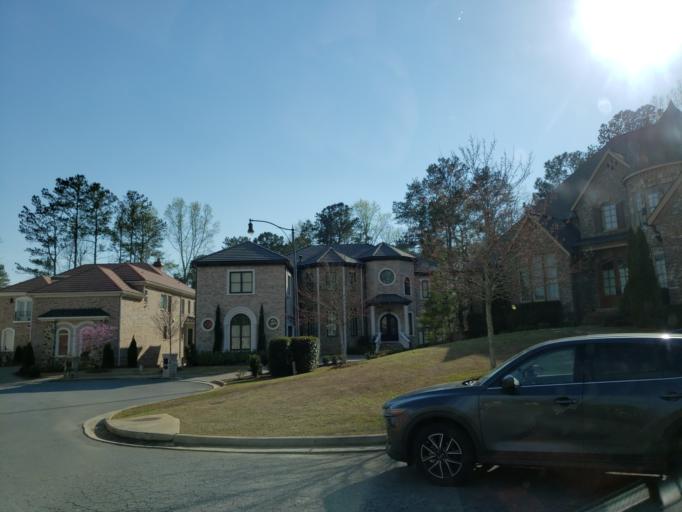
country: US
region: Georgia
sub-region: Cobb County
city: Marietta
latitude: 33.9773
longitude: -84.4726
